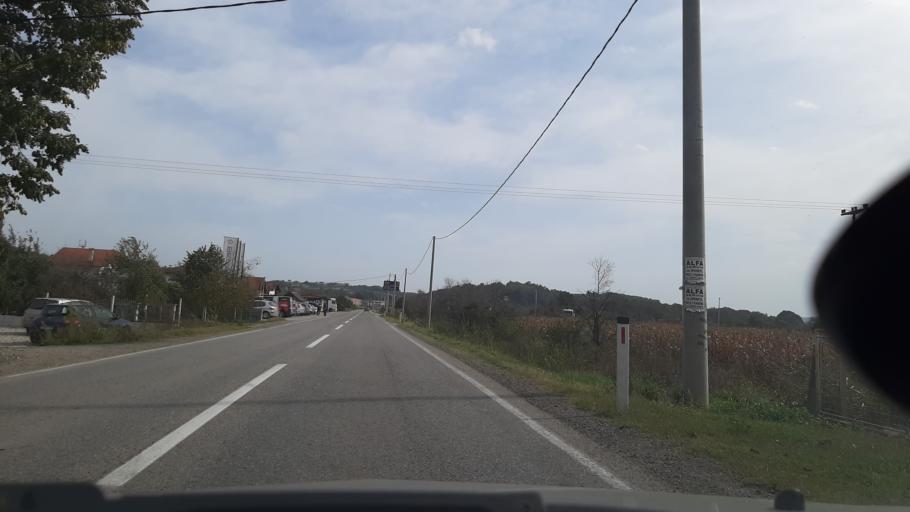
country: BA
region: Republika Srpska
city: Laktasi
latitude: 44.8772
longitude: 17.3020
